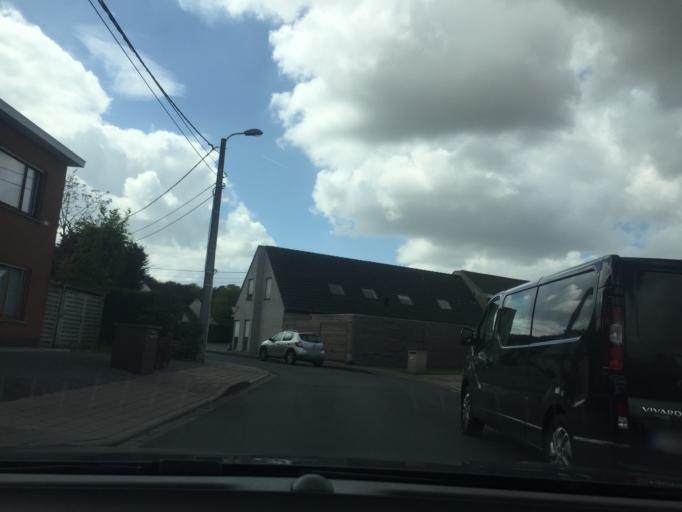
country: BE
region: Flanders
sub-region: Provincie West-Vlaanderen
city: Roeselare
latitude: 50.9310
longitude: 3.1387
